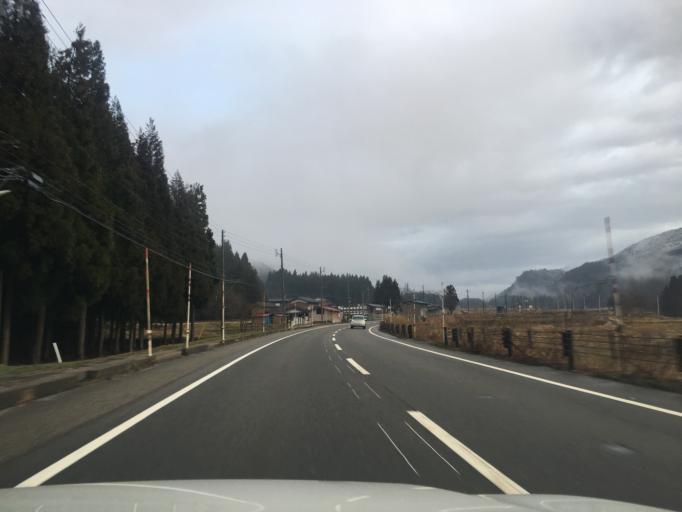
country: JP
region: Niigata
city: Murakami
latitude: 38.3522
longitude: 139.5504
